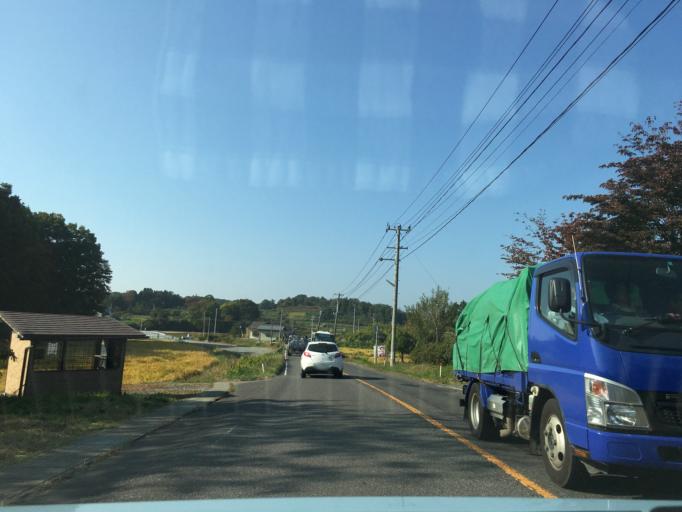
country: JP
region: Fukushima
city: Sukagawa
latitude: 37.2800
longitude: 140.3208
